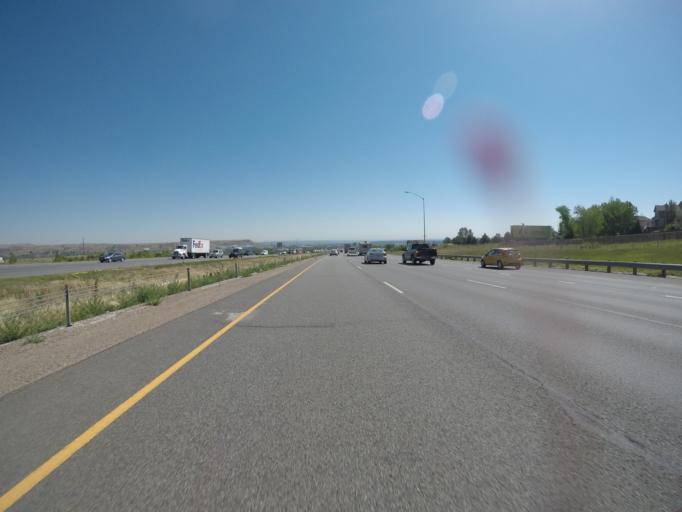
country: US
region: Colorado
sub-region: Jefferson County
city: West Pleasant View
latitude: 39.7202
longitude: -105.1870
